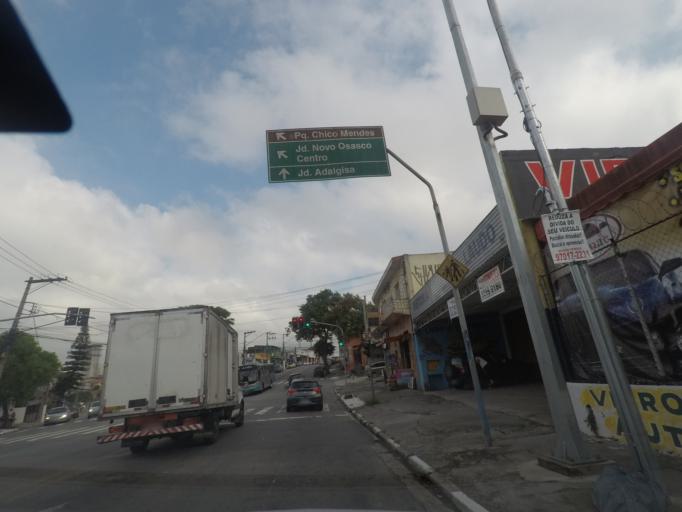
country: BR
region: Sao Paulo
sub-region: Osasco
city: Osasco
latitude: -23.5657
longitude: -46.7810
